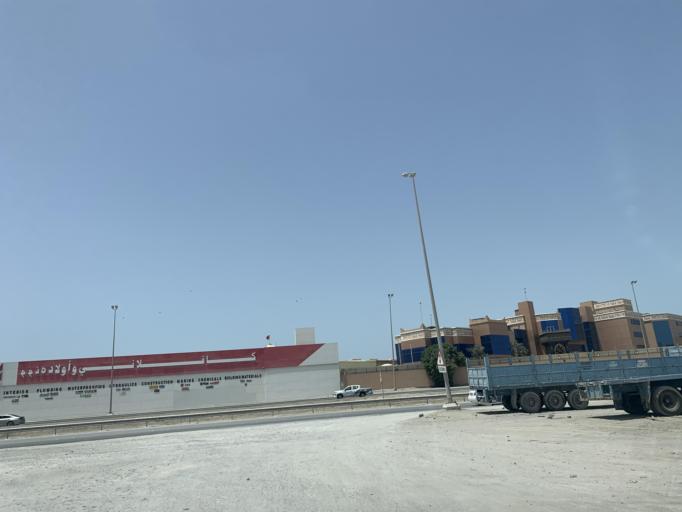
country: BH
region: Northern
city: Sitrah
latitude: 26.1770
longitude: 50.6073
